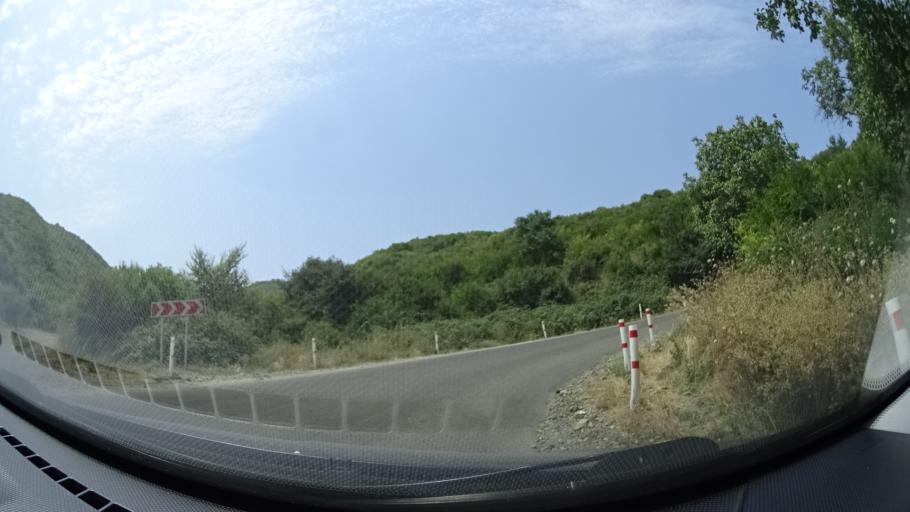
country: GE
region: Kakheti
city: Sighnaghi
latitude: 41.6217
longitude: 45.9366
